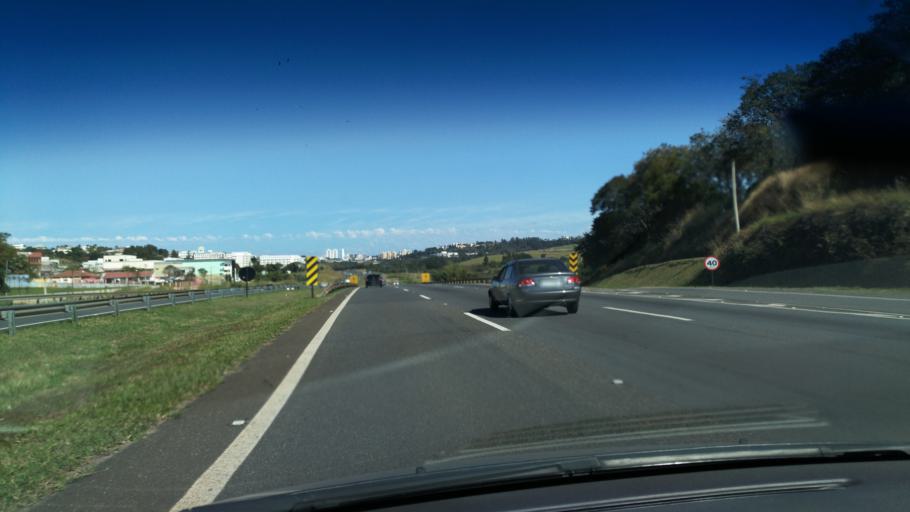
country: BR
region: Sao Paulo
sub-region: Campinas
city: Campinas
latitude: -22.8106
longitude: -47.0345
